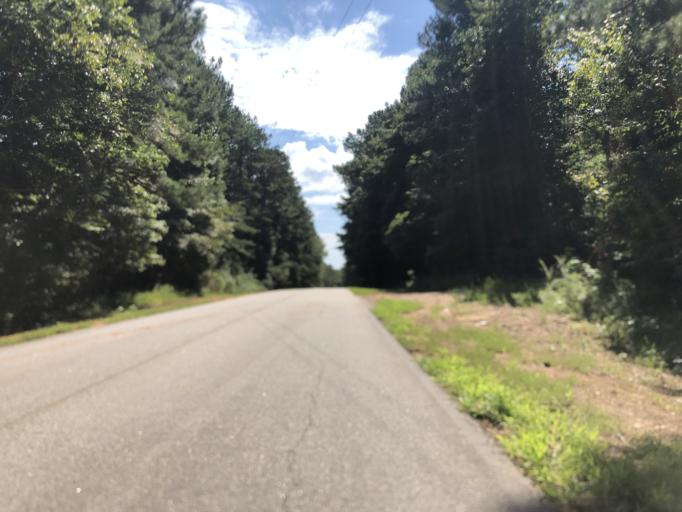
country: US
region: Georgia
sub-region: Heard County
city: Franklin
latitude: 33.3684
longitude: -85.0141
